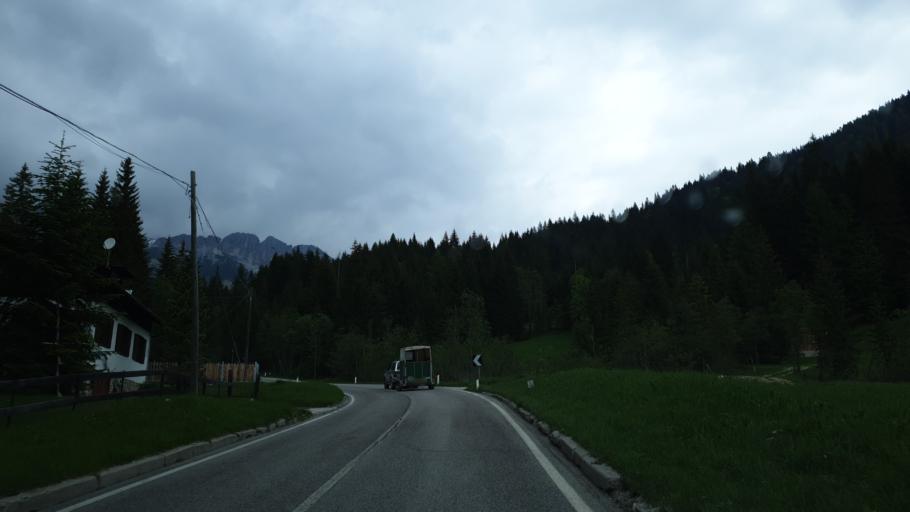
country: IT
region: Veneto
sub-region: Provincia di Belluno
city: San Vito
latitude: 46.5501
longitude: 12.2477
